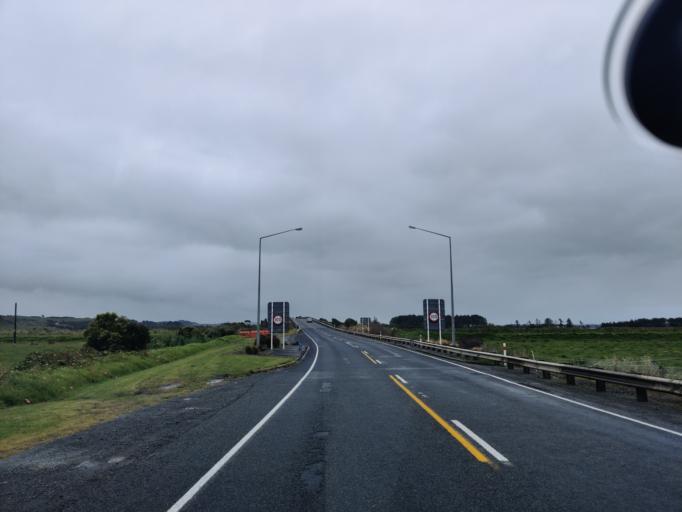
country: NZ
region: Northland
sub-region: Kaipara District
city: Dargaville
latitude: -35.9365
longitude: 173.8821
